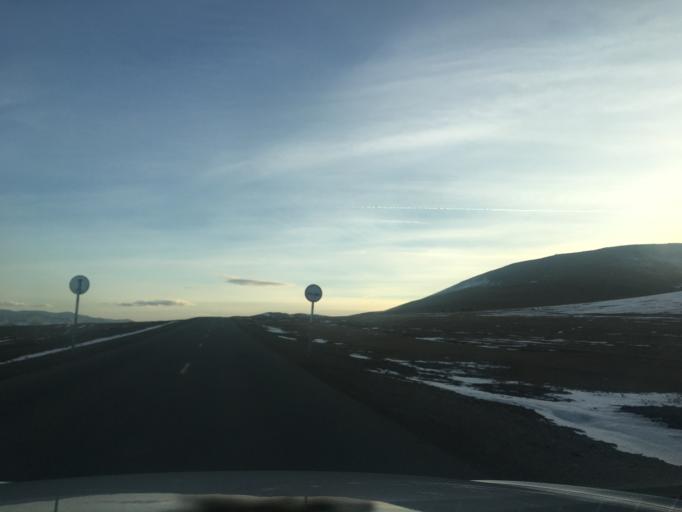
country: MN
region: Central Aimak
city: Mandal
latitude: 48.2260
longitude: 106.7158
